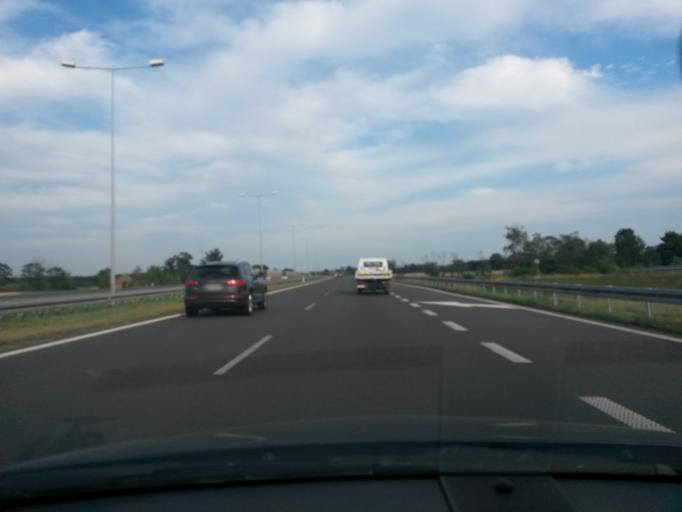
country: PL
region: Greater Poland Voivodeship
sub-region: Powiat turecki
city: Brudzew
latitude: 52.1330
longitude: 18.6417
